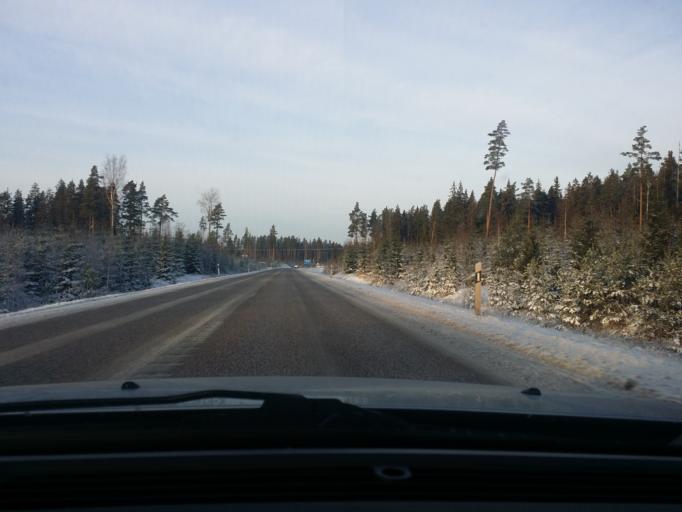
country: SE
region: OErebro
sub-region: Lindesbergs Kommun
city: Frovi
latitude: 59.4758
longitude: 15.3889
